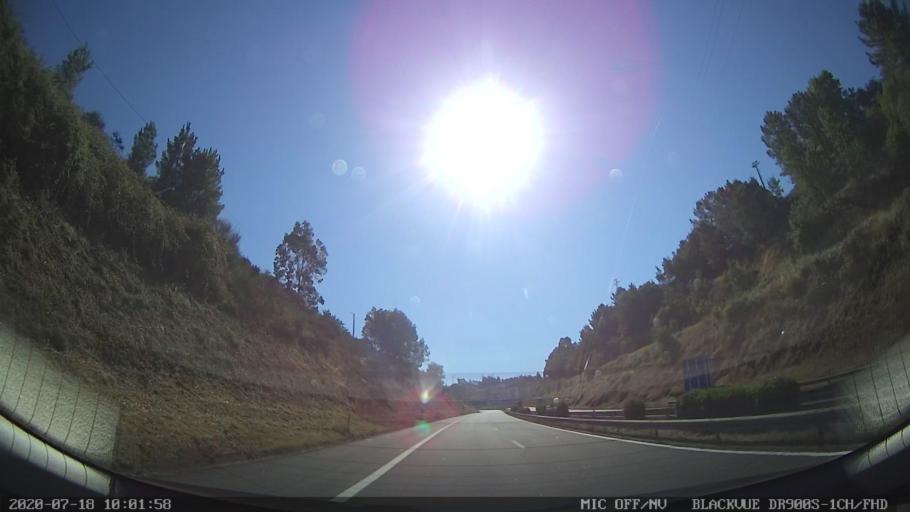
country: PT
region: Porto
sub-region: Penafiel
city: Penafiel
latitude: 41.2146
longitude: -8.2796
